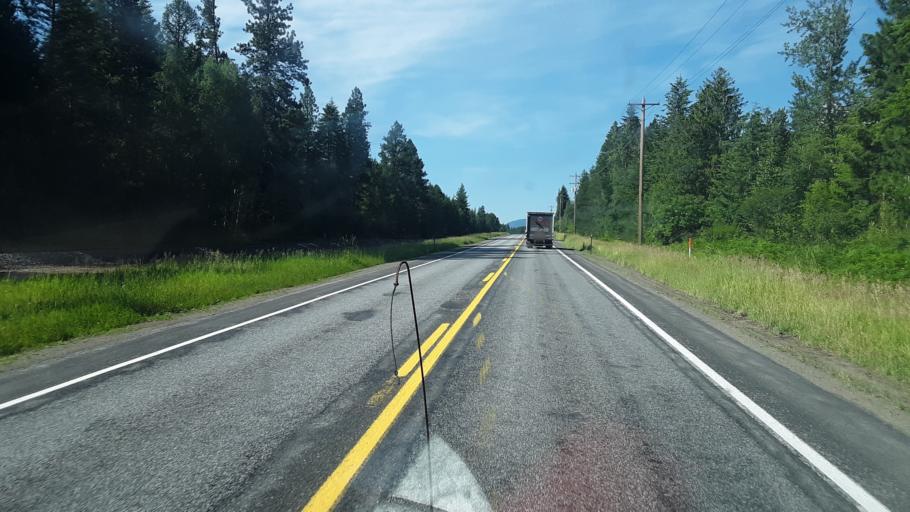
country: US
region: Idaho
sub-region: Bonner County
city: Ponderay
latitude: 48.4996
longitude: -116.4499
